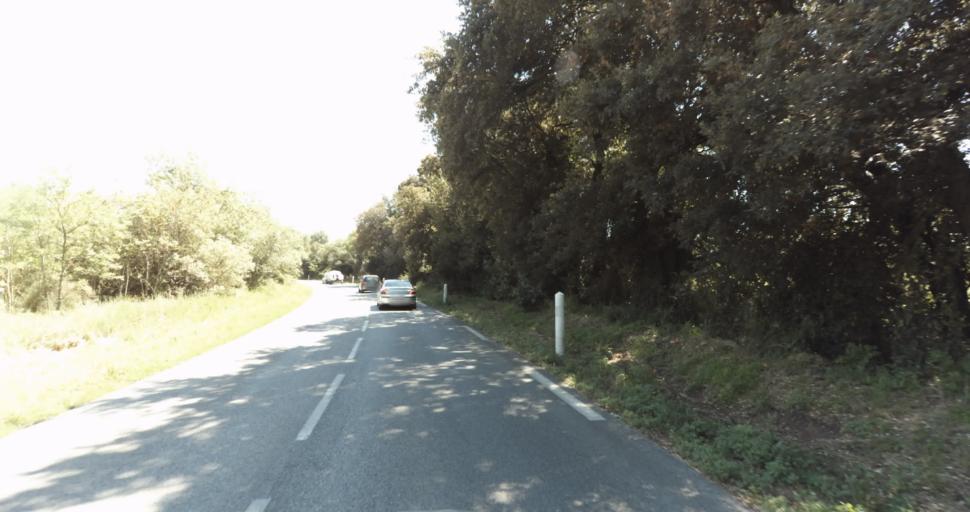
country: FR
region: Provence-Alpes-Cote d'Azur
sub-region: Departement du Var
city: Hyeres
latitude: 43.1351
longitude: 6.1579
